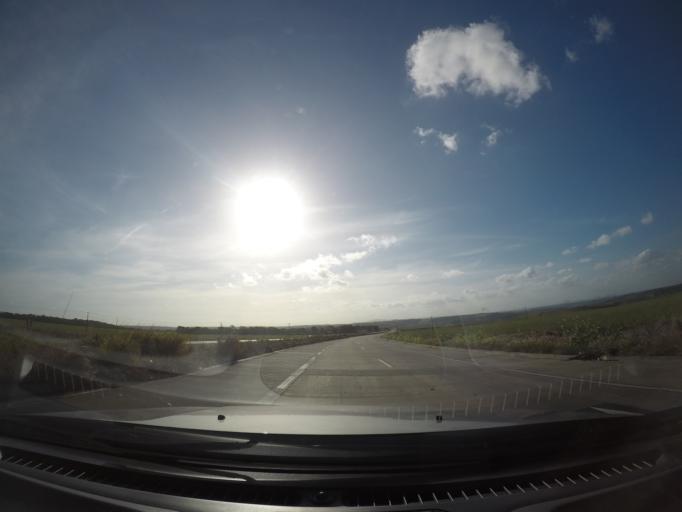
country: BR
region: Alagoas
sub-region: Pilar
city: Pilar
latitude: -9.5867
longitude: -35.9796
